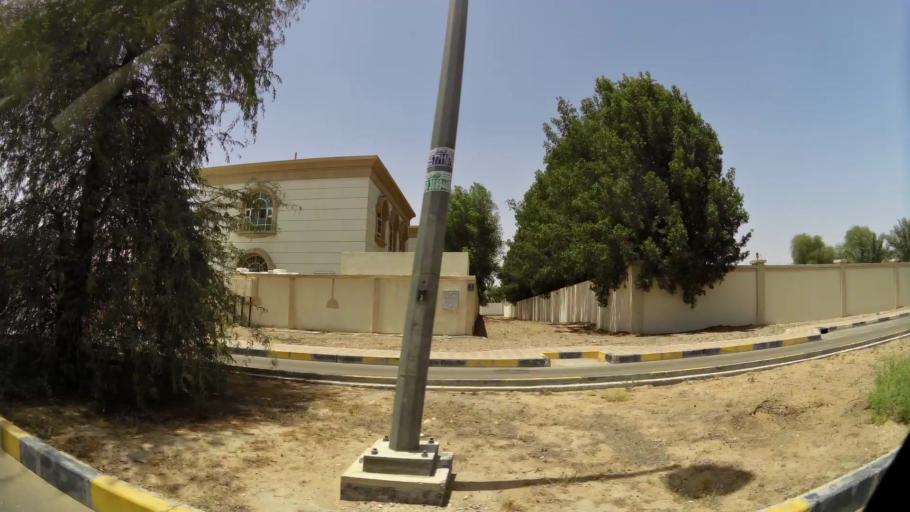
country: OM
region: Al Buraimi
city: Al Buraymi
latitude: 24.2547
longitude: 55.7175
